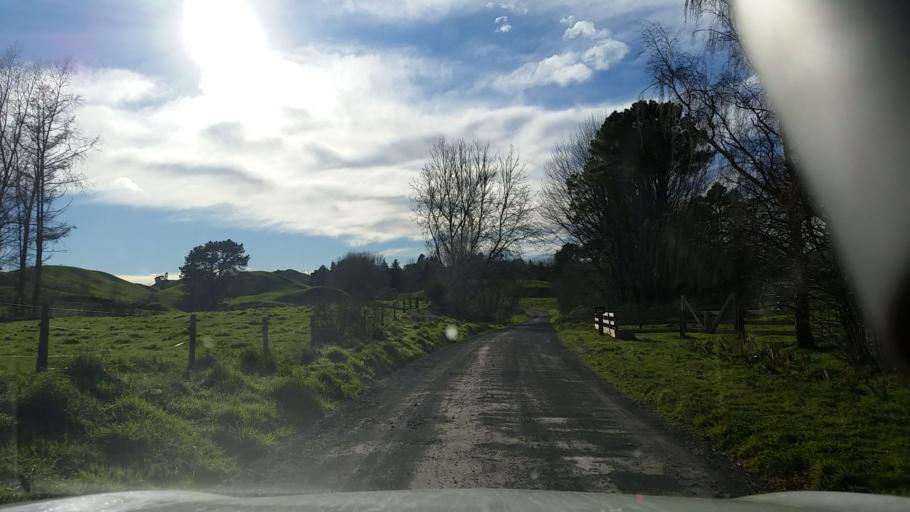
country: NZ
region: Waikato
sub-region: South Waikato District
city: Tokoroa
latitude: -38.3850
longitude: 176.0788
